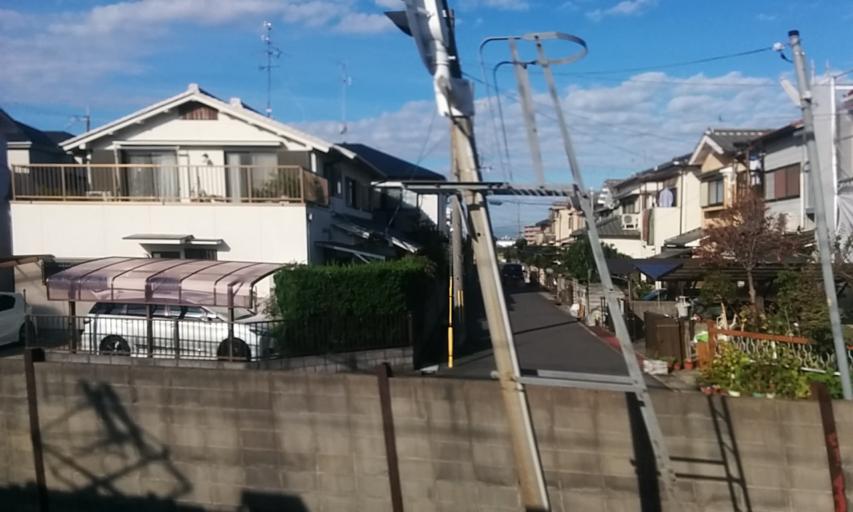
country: JP
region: Kyoto
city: Tanabe
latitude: 34.8583
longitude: 135.7733
